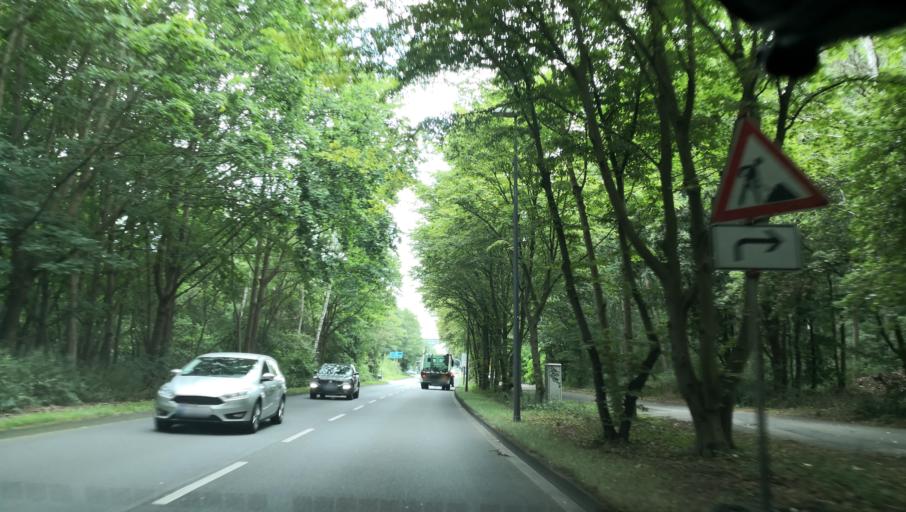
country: DE
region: North Rhine-Westphalia
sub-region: Regierungsbezirk Koln
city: Mengenich
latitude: 50.9762
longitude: 6.8750
